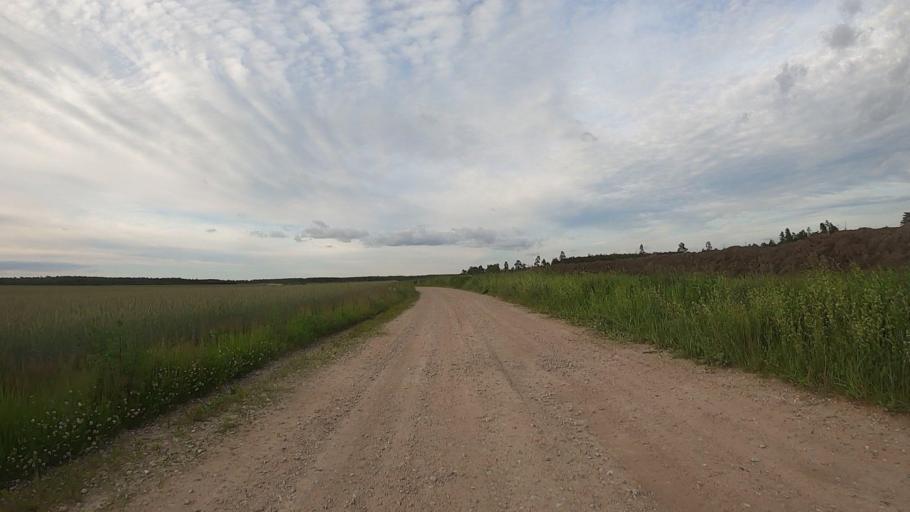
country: LV
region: Olaine
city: Olaine
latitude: 56.8154
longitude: 23.9496
